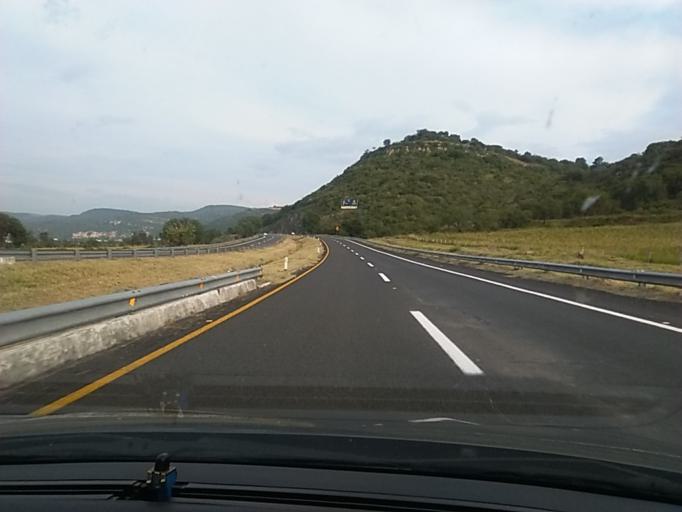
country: MX
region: Michoacan
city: Copandaro de Galeana
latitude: 19.8830
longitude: -101.2228
